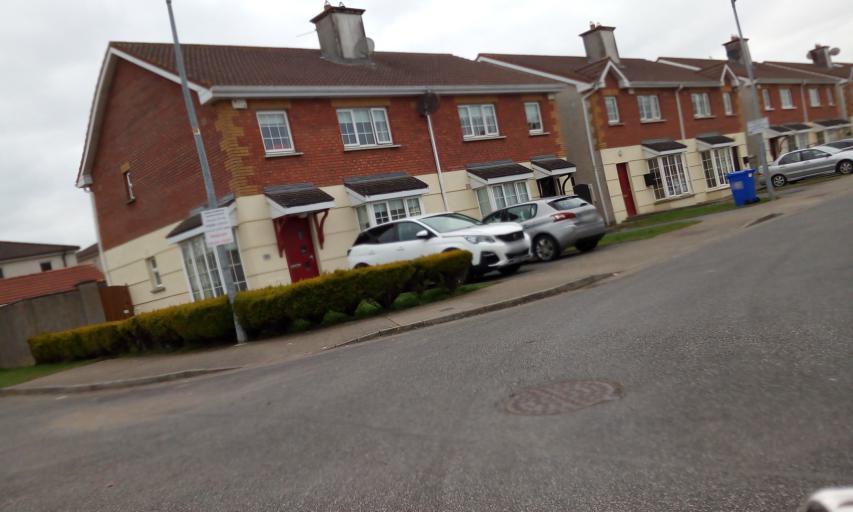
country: IE
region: Leinster
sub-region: Kilkenny
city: Kilkenny
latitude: 52.6678
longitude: -7.2317
